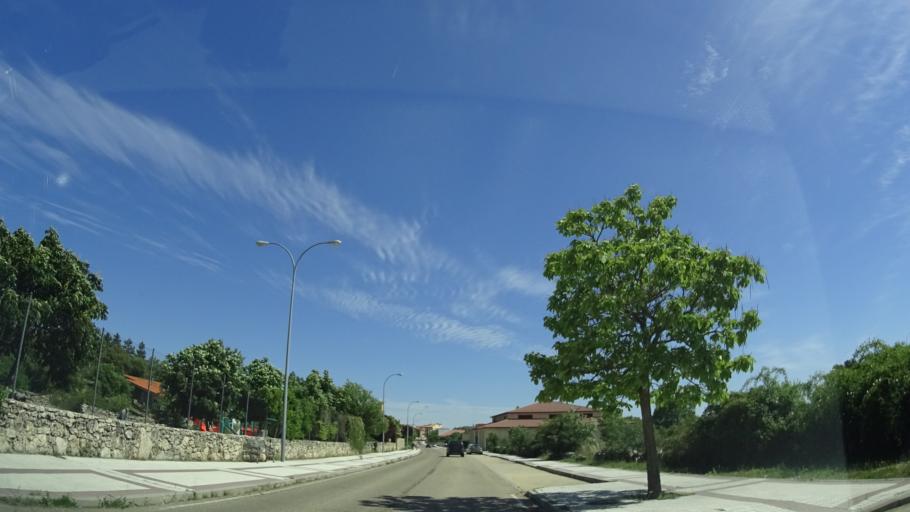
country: ES
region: Castille and Leon
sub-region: Provincia de Segovia
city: Pradena
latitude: 41.1335
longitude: -3.6888
